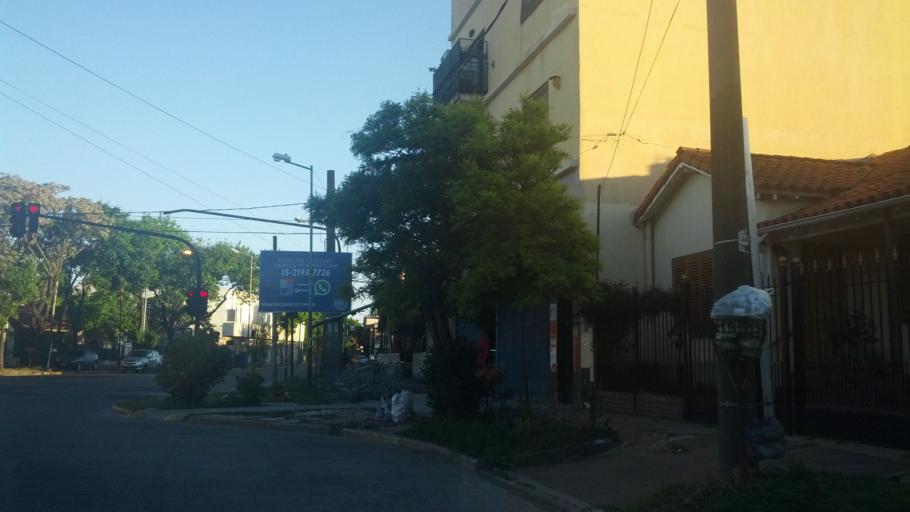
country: AR
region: Buenos Aires
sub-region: Partido de Almirante Brown
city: Adrogue
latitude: -34.7814
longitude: -58.3901
